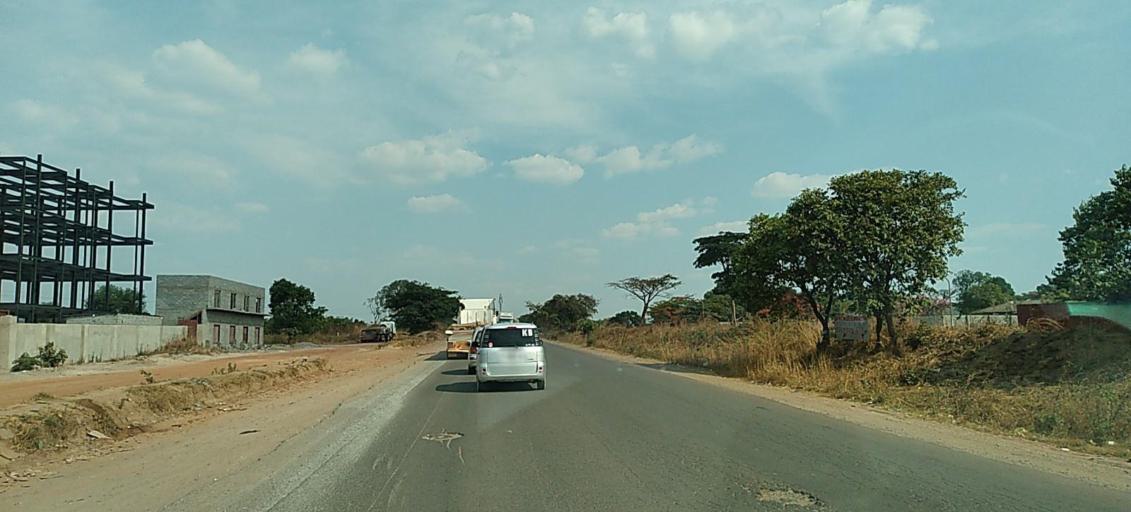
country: ZM
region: Copperbelt
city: Chililabombwe
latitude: -12.3632
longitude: 27.8515
